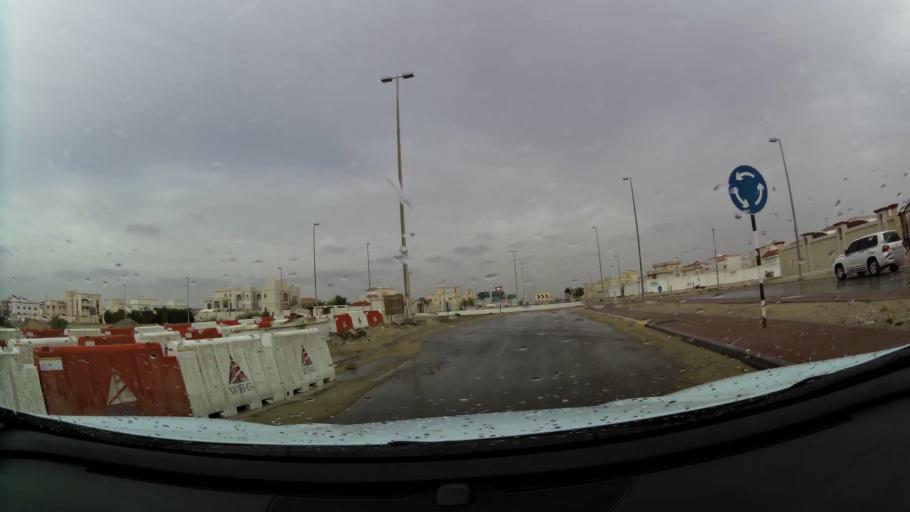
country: AE
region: Abu Dhabi
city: Abu Dhabi
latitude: 24.3560
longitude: 54.6275
